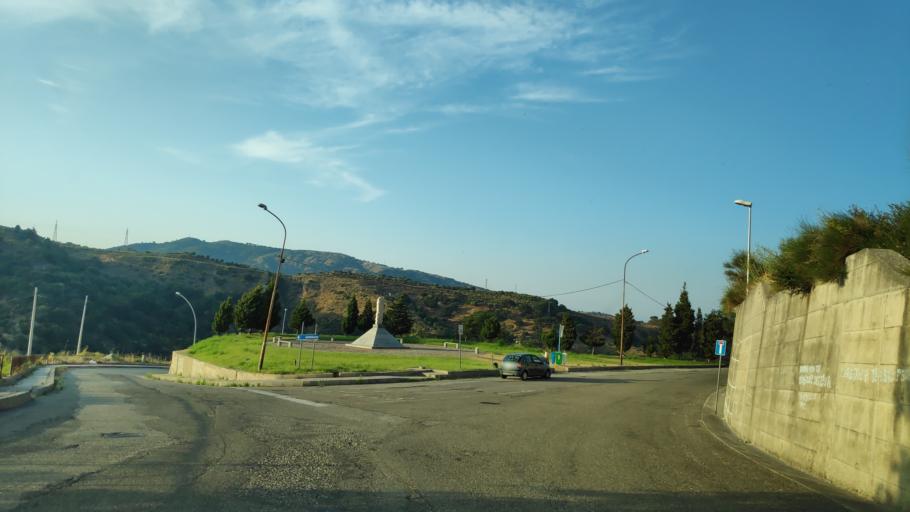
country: IT
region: Calabria
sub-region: Provincia di Catanzaro
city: Satriano
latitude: 38.6696
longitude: 16.4814
